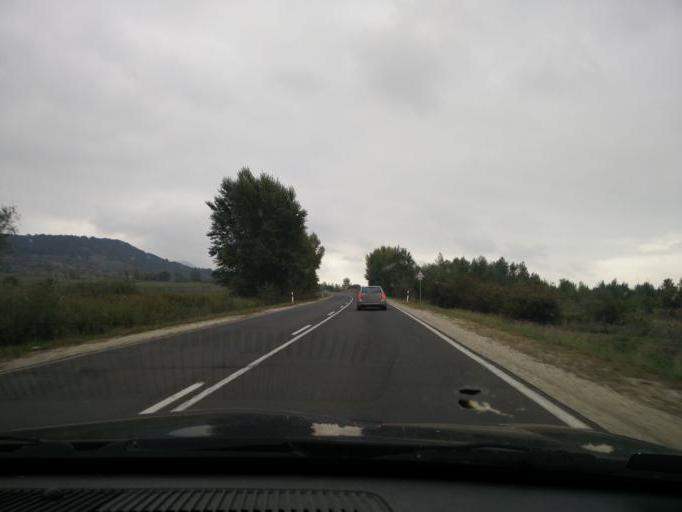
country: HU
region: Komarom-Esztergom
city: Dorog
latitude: 47.7396
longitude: 18.7454
